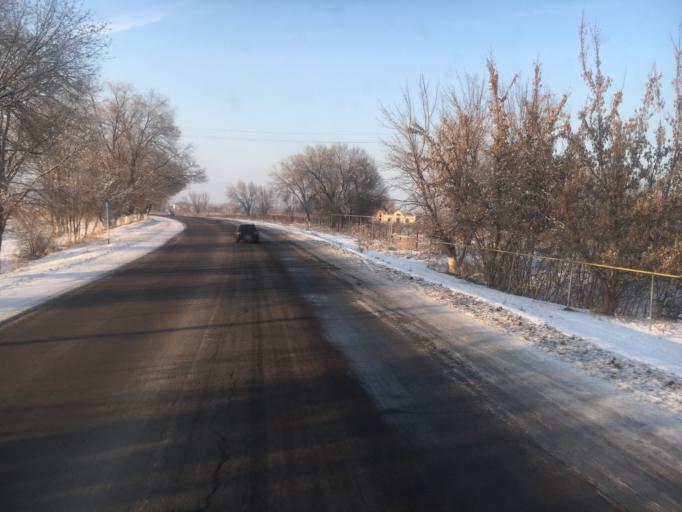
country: KZ
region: Almaty Oblysy
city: Burunday
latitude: 43.3403
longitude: 76.6587
